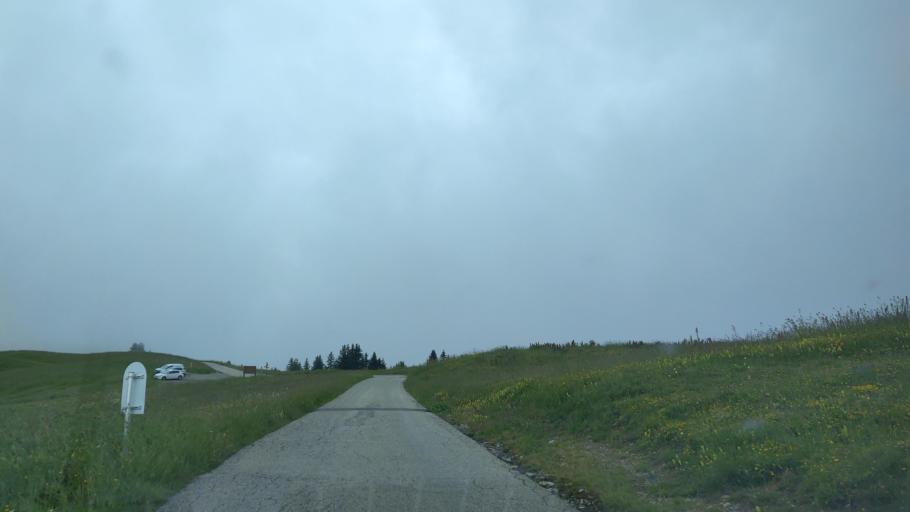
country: FR
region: Rhone-Alpes
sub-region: Departement de la Savoie
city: Beaufort
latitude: 45.7493
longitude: 6.5180
